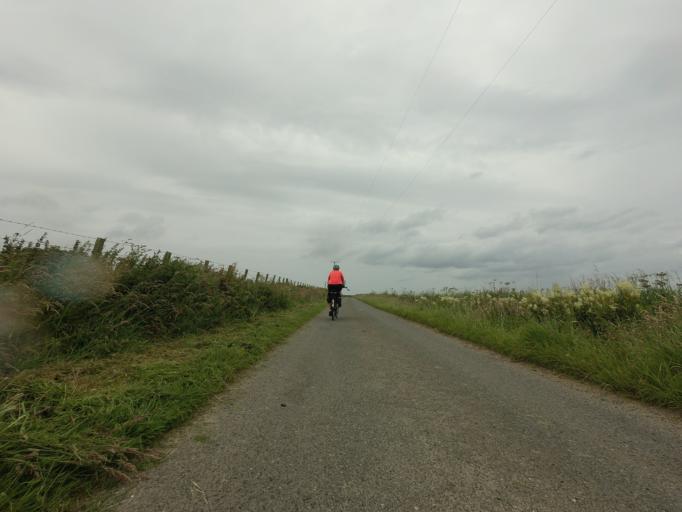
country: GB
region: Scotland
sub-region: Moray
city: Cullen
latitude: 57.6686
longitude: -2.7676
